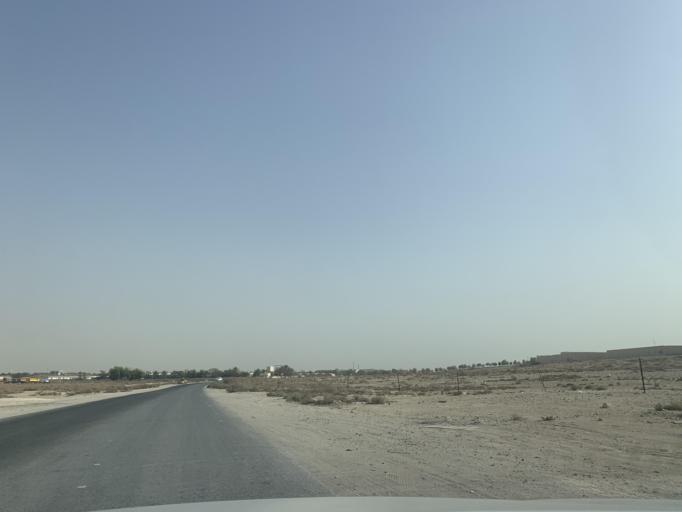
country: BH
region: Central Governorate
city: Madinat Hamad
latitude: 26.1612
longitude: 50.4881
